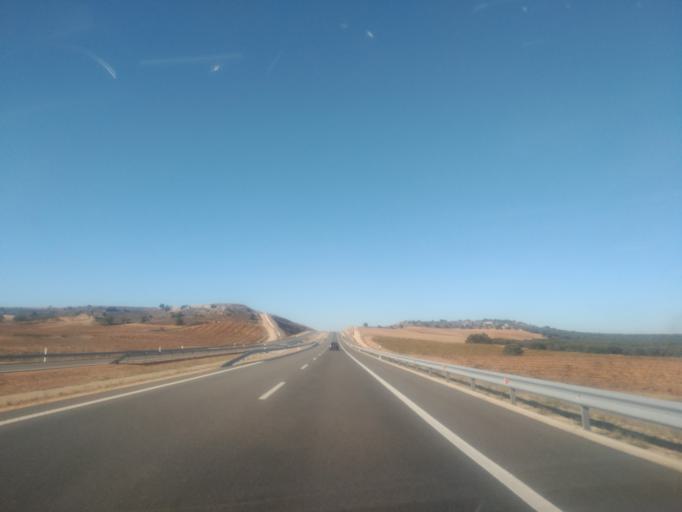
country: ES
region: Castille and Leon
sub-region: Provincia de Burgos
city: Campillo de Aranda
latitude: 41.6338
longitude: -3.7367
